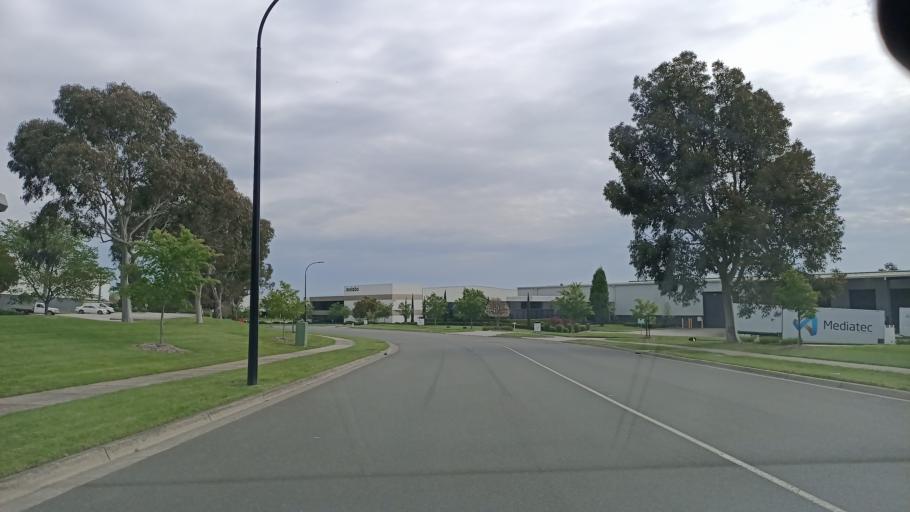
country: AU
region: Victoria
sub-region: Knox
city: Scoresby
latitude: -37.9037
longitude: 145.2189
